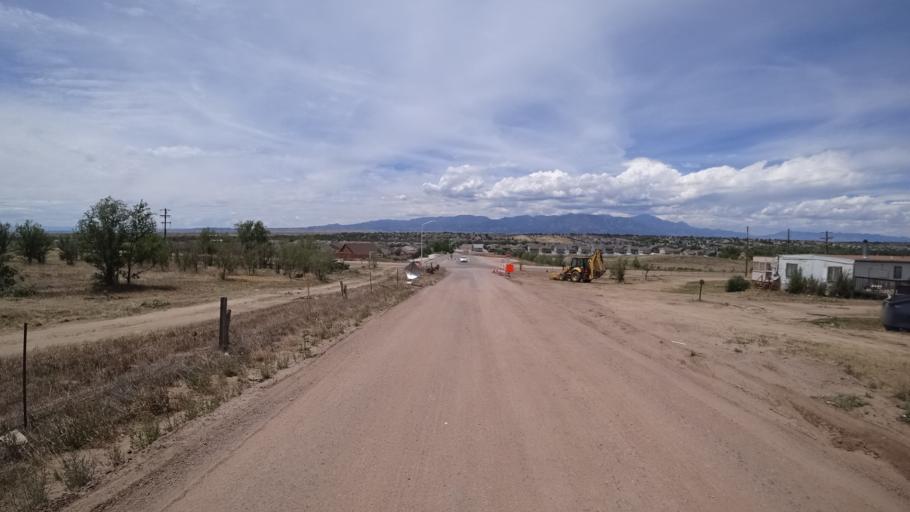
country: US
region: Colorado
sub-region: El Paso County
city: Fountain
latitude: 38.6940
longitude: -104.6728
